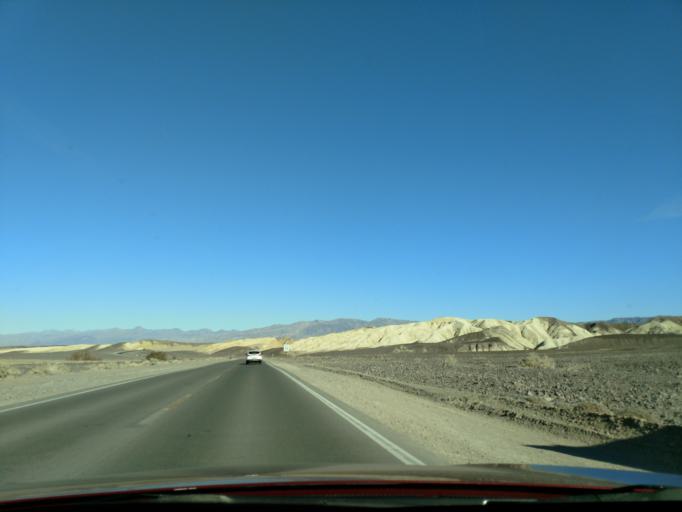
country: US
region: Nevada
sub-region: Nye County
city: Beatty
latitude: 36.4753
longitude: -116.8678
